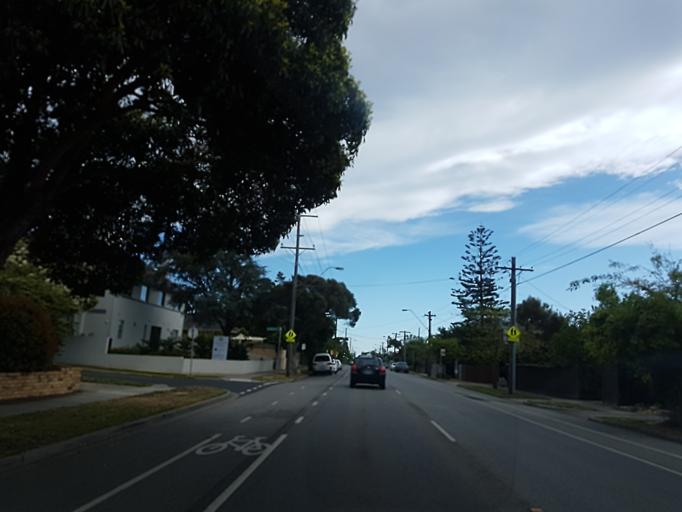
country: AU
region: Victoria
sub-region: Glen Eira
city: Caulfield
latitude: -37.8802
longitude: 145.0162
